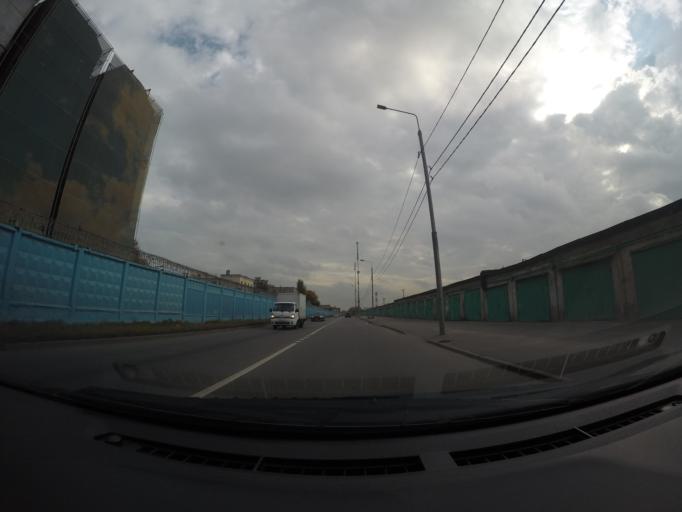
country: RU
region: Moscow
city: Lefortovo
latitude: 55.7735
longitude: 37.7149
